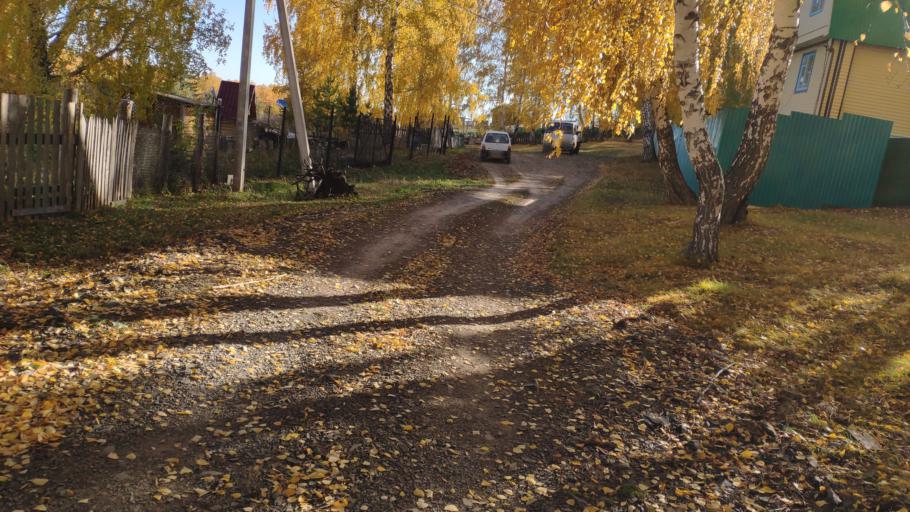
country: RU
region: Bashkortostan
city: Abzakovo
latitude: 53.3440
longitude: 58.5030
